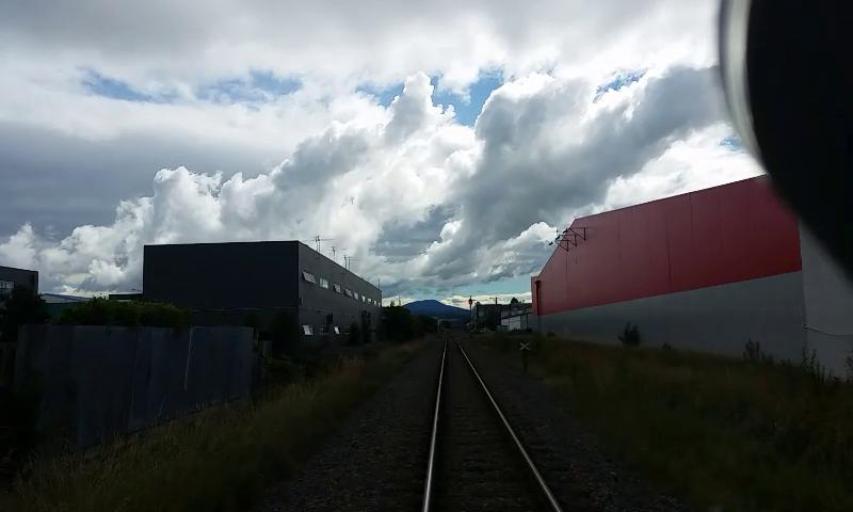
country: NZ
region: Canterbury
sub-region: Waimakariri District
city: Woodend
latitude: -43.3049
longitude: 172.5987
